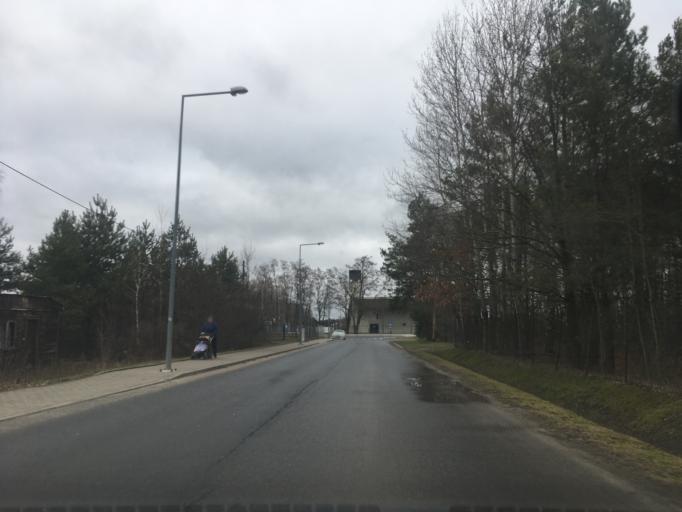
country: PL
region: Masovian Voivodeship
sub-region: Powiat piaseczynski
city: Lesznowola
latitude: 52.0559
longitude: 20.8956
